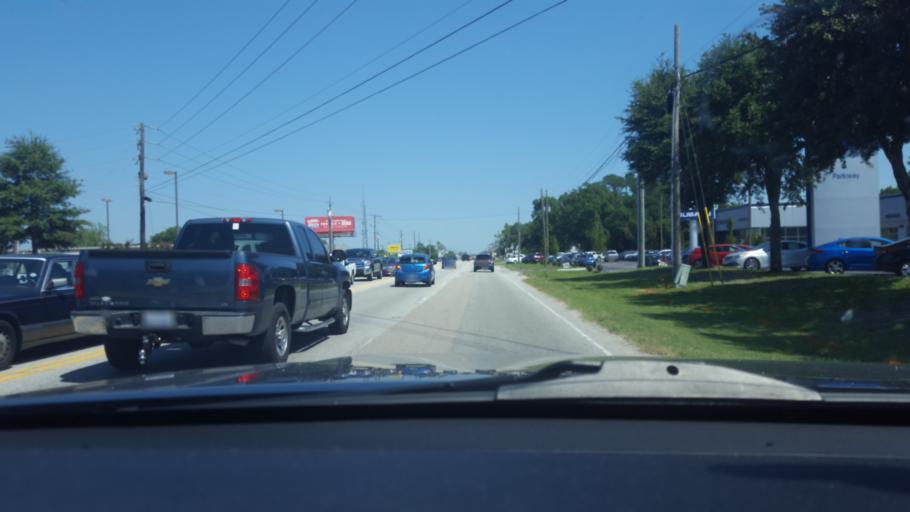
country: US
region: North Carolina
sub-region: New Hanover County
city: Kings Grant
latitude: 34.2505
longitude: -77.8567
